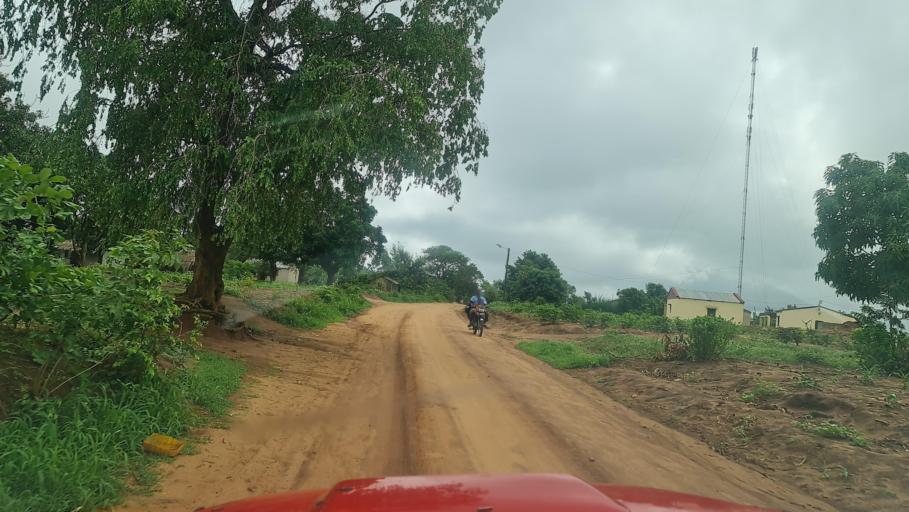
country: MW
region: Southern Region
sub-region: Nsanje District
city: Nsanje
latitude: -17.1910
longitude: 35.7068
